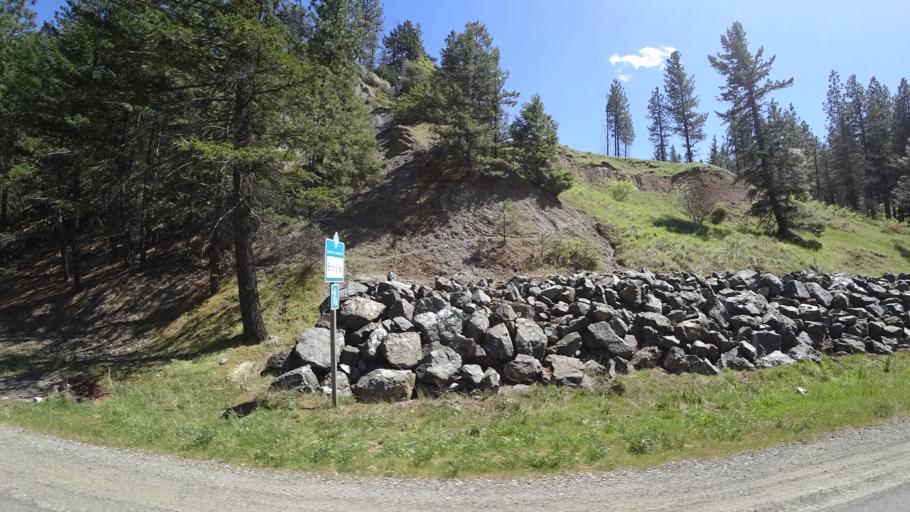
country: US
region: California
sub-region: Trinity County
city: Weaverville
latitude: 40.7384
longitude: -122.9836
